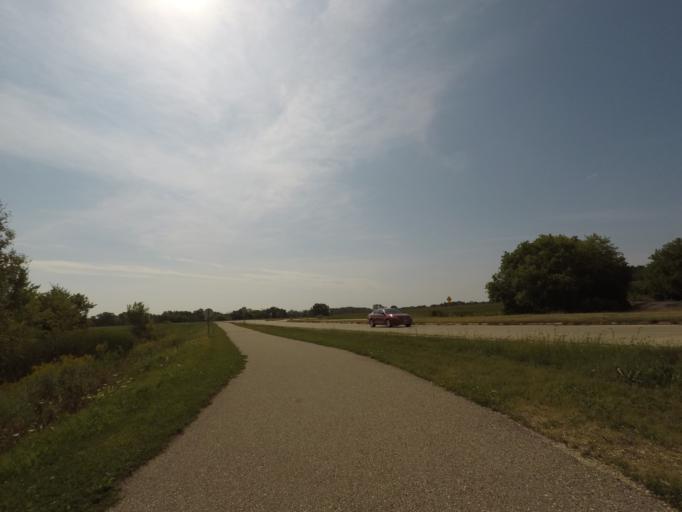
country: US
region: Wisconsin
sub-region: Jefferson County
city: Fort Atkinson
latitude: 42.9513
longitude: -88.8287
